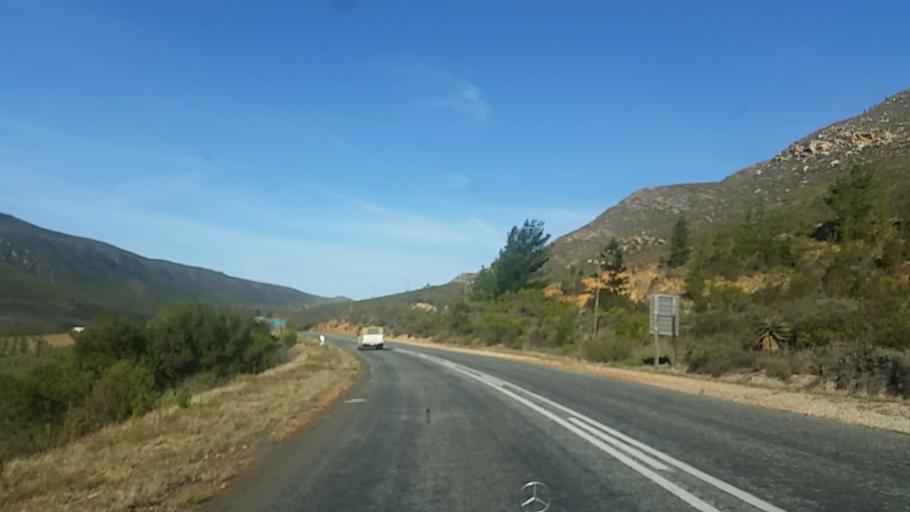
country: ZA
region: Western Cape
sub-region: Eden District Municipality
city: Knysna
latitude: -33.7467
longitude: 22.9846
